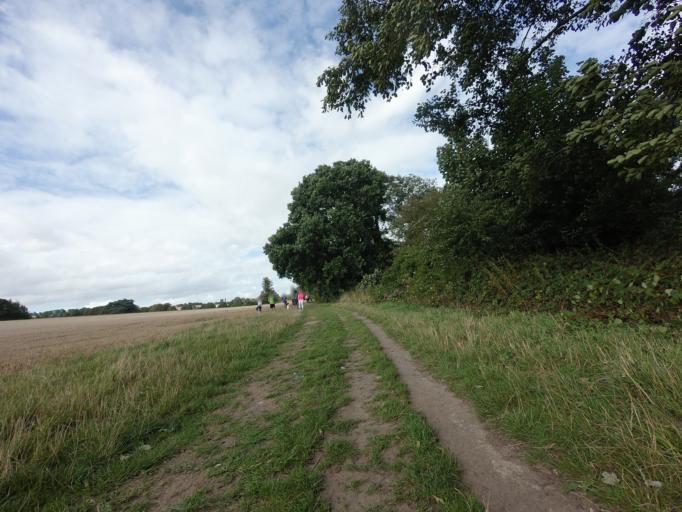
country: GB
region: England
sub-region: Kent
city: Eynsford
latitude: 51.3560
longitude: 0.1927
